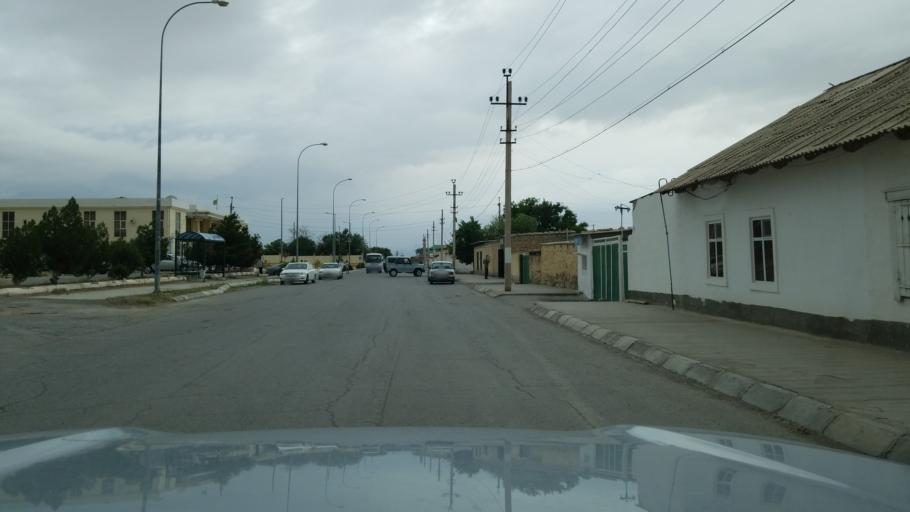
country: TM
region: Balkan
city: Serdar
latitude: 38.9728
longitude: 56.2820
